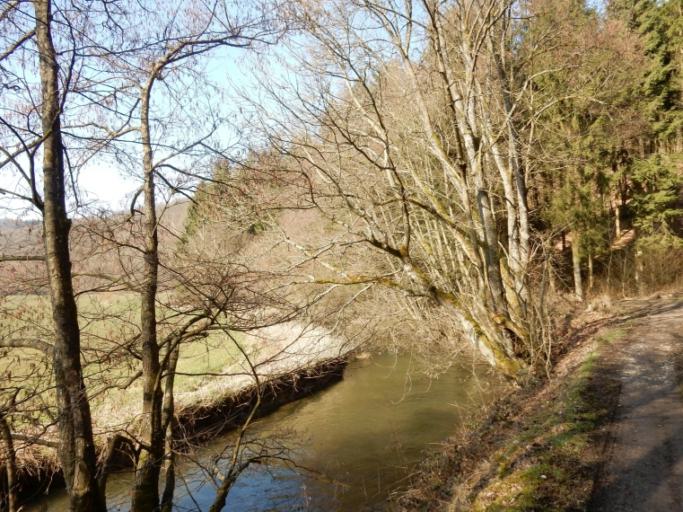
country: LU
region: Diekirch
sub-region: Canton de Wiltz
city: Winseler
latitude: 49.9734
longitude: 5.8821
